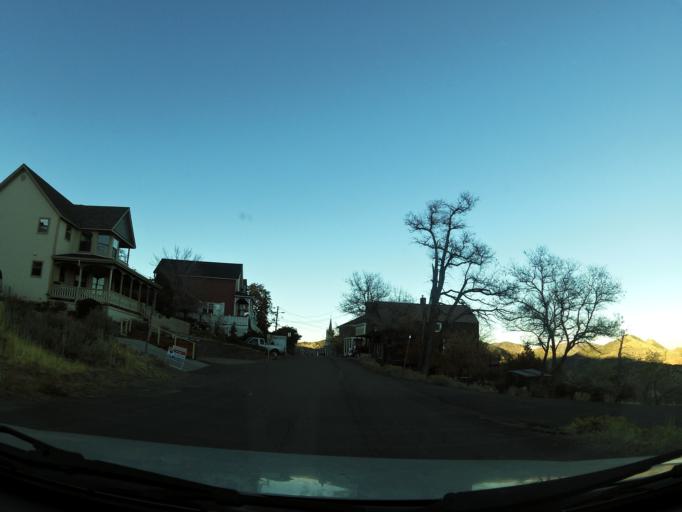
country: US
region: Nevada
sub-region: Storey County
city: Virginia City
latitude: 39.3058
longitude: -119.6508
